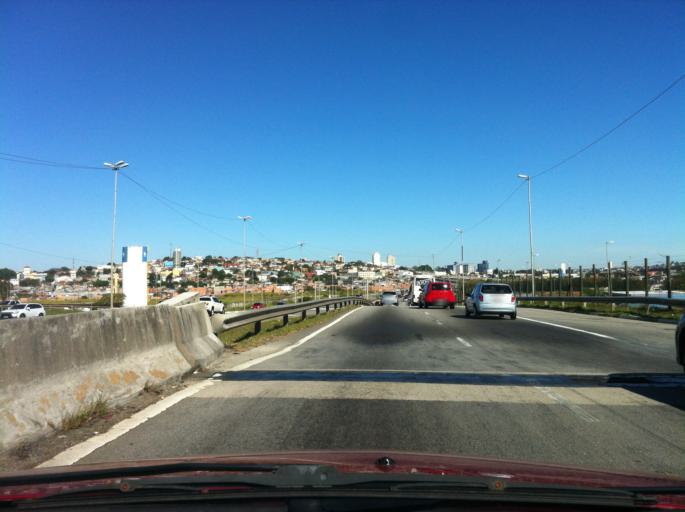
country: BR
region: Sao Paulo
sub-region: Guarulhos
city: Guarulhos
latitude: -23.4831
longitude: -46.4533
